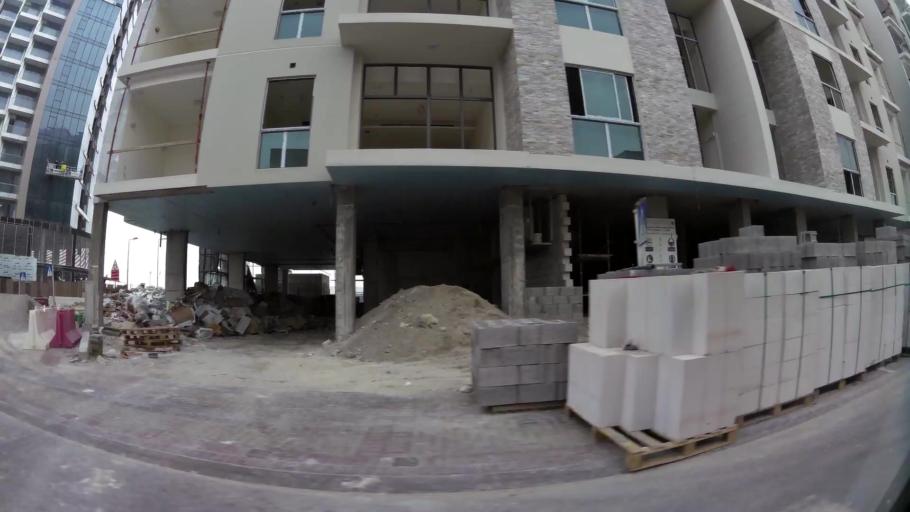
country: BH
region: Central Governorate
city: Dar Kulayb
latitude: 25.8689
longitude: 50.6096
